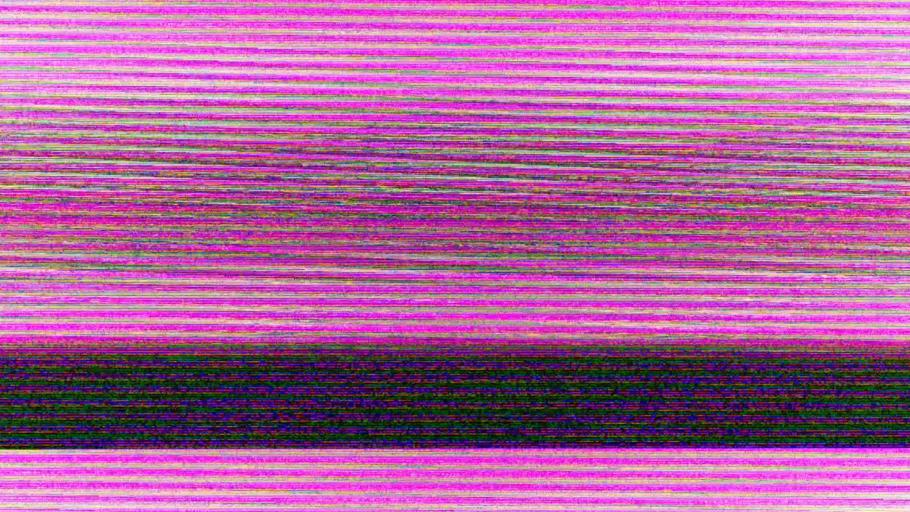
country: US
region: Massachusetts
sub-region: Middlesex County
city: Shirley
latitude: 42.5268
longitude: -71.6307
